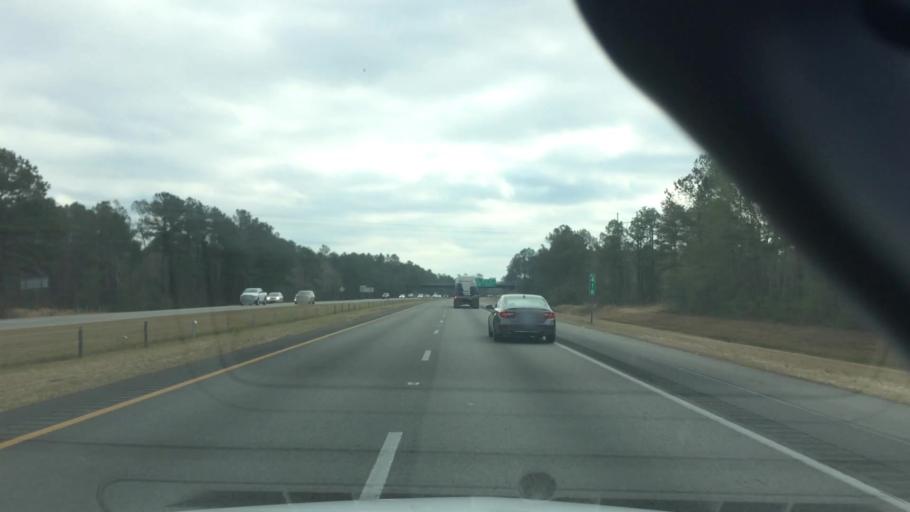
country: US
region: North Carolina
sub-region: New Hanover County
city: Skippers Corner
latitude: 34.3314
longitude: -77.8750
